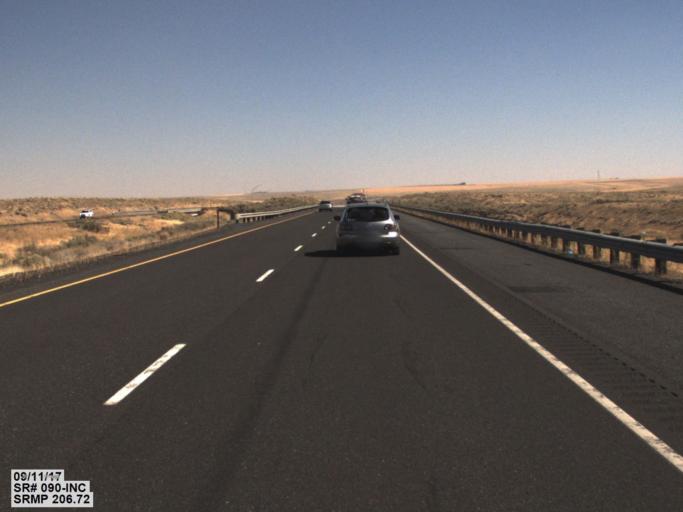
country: US
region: Washington
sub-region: Adams County
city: Ritzville
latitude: 47.0969
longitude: -118.6706
